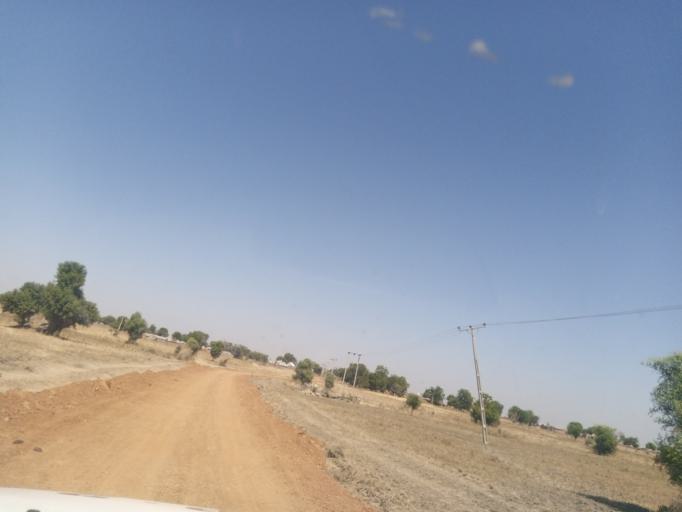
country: NG
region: Adamawa
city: Yola
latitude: 9.3071
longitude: 12.8897
